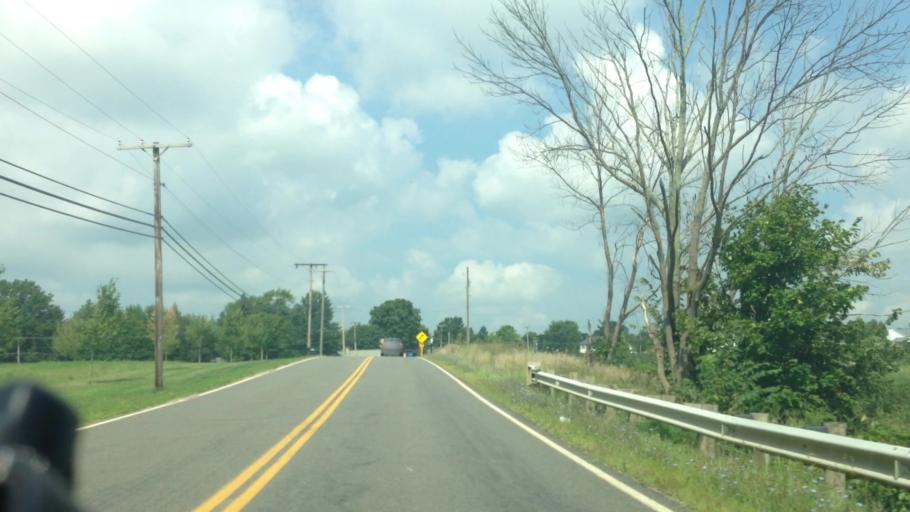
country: US
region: Ohio
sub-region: Stark County
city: Canal Fulton
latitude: 40.8493
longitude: -81.6253
